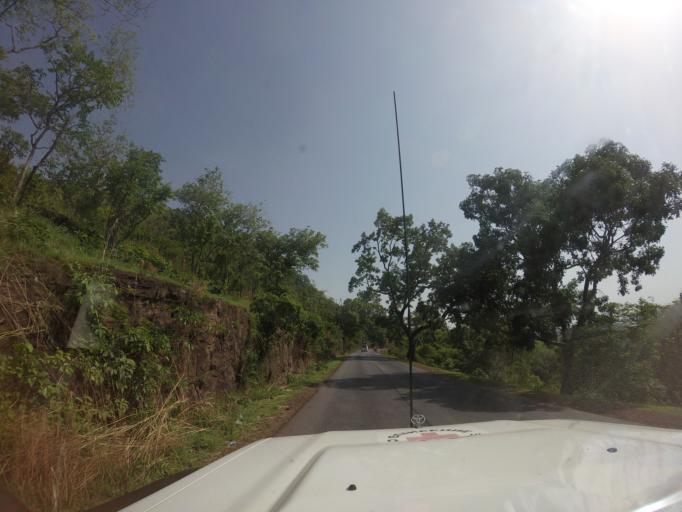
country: GN
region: Kindia
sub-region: Kindia
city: Kindia
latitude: 10.0106
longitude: -12.8024
